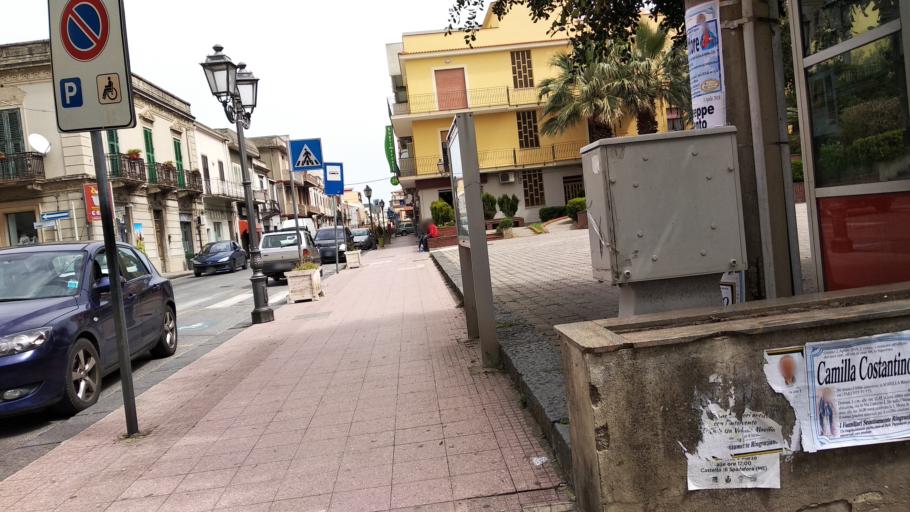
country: IT
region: Sicily
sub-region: Messina
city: Spadafora
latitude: 38.2223
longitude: 15.3793
